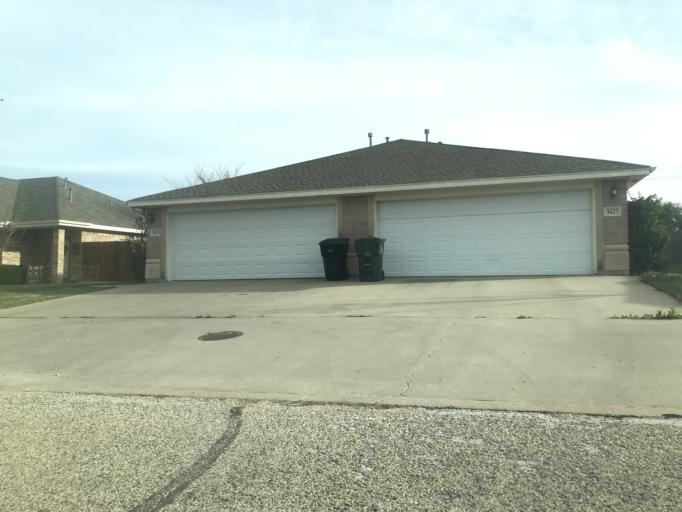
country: US
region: Texas
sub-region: Taylor County
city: Abilene
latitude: 32.3954
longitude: -99.7706
